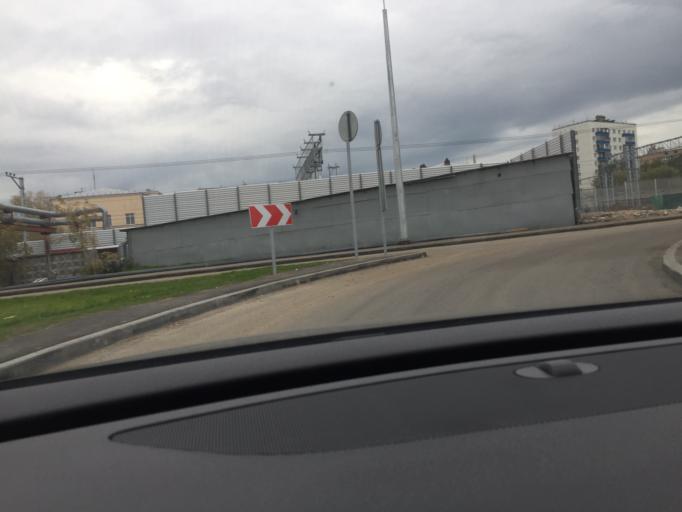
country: RU
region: Moskovskaya
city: Bogorodskoye
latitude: 55.7984
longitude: 37.7475
